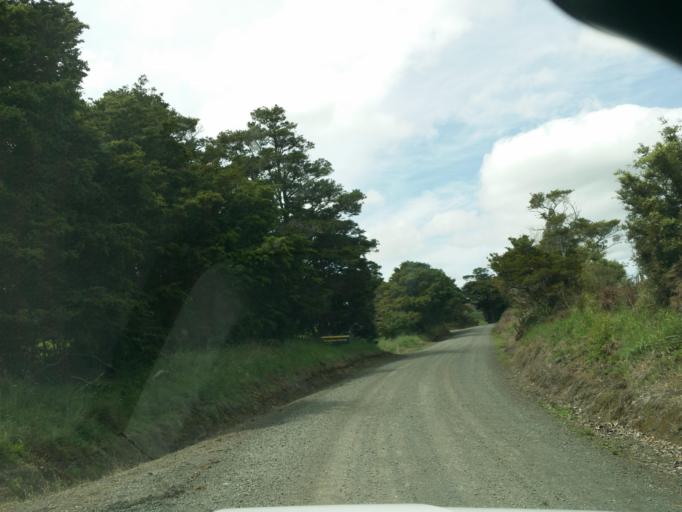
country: NZ
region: Northland
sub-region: Whangarei
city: Maungatapere
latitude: -35.9056
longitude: 174.1367
